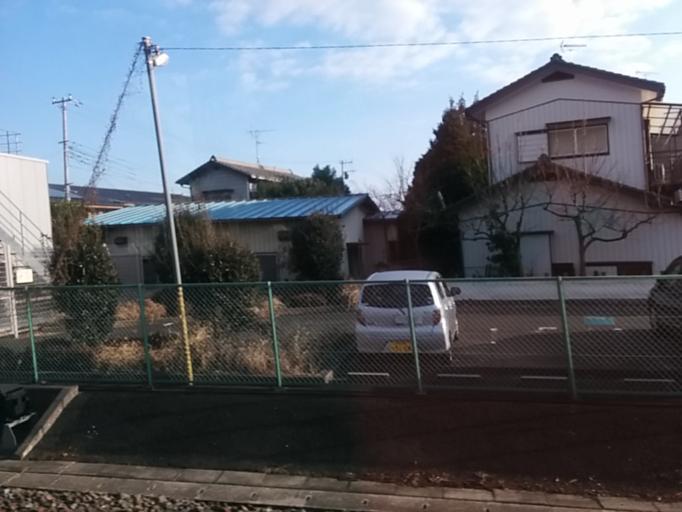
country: JP
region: Saitama
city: Oi
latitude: 35.8580
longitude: 139.5255
